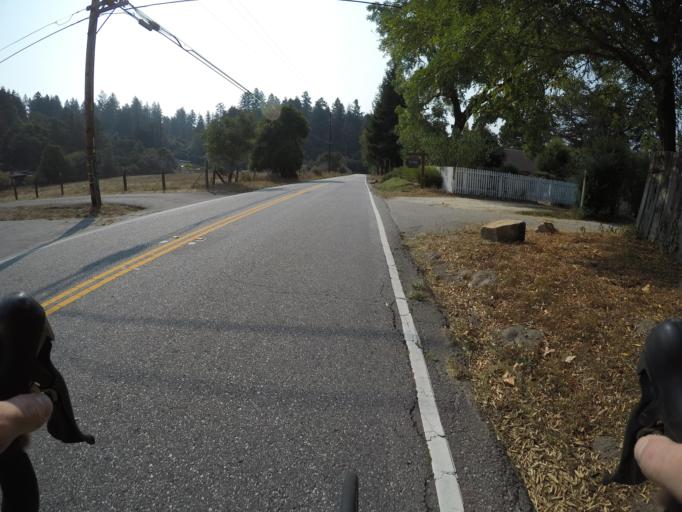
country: US
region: California
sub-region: Santa Cruz County
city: Scotts Valley
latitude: 37.0339
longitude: -122.0177
